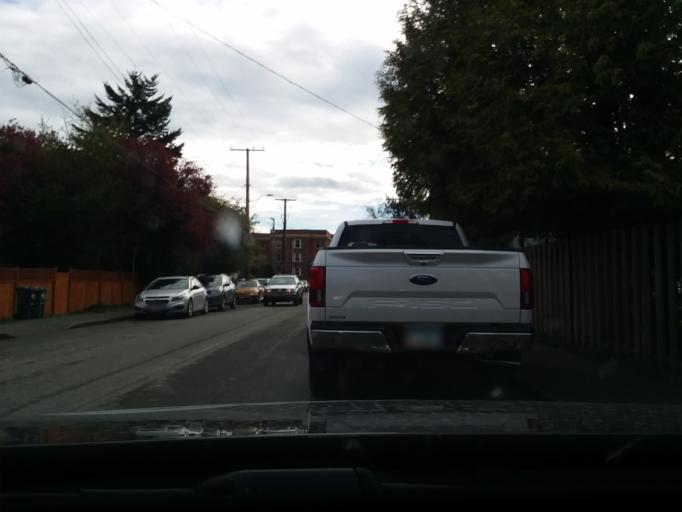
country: CA
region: British Columbia
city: Oak Bay
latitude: 48.4309
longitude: -123.3313
